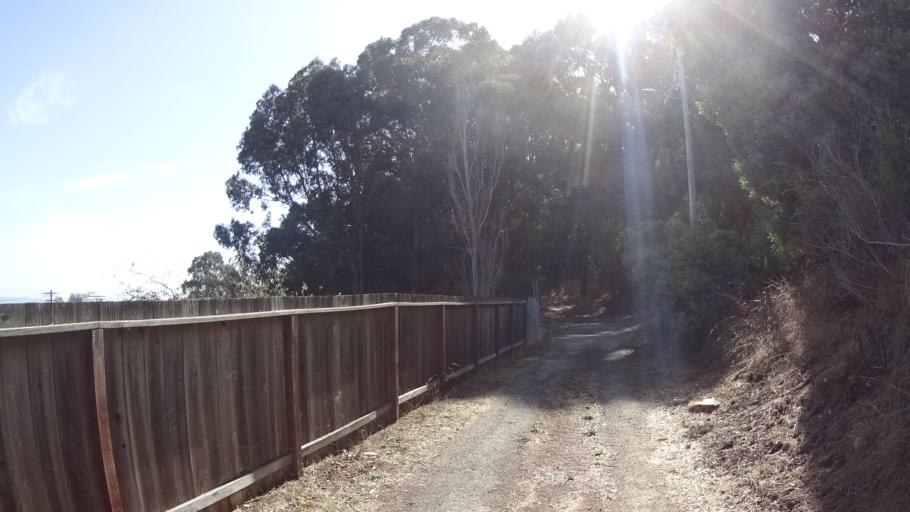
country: US
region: California
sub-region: San Mateo County
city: Brisbane
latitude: 37.6773
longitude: -122.3939
